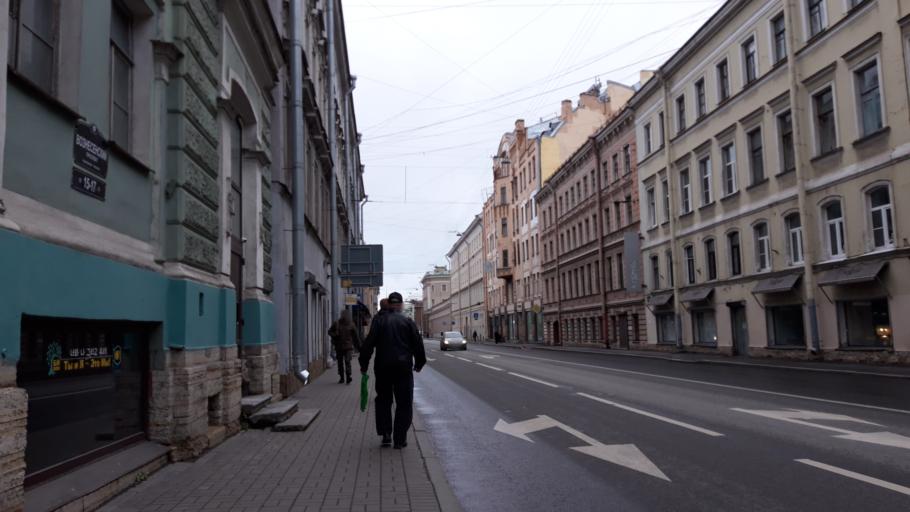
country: RU
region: St.-Petersburg
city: Saint Petersburg
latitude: 59.9284
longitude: 30.3083
